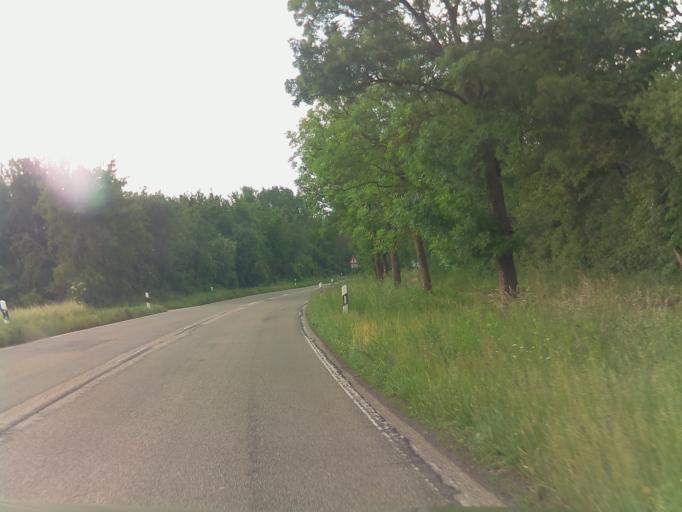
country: DE
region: Rheinland-Pfalz
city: Zeiskam
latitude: 49.2238
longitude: 8.2497
